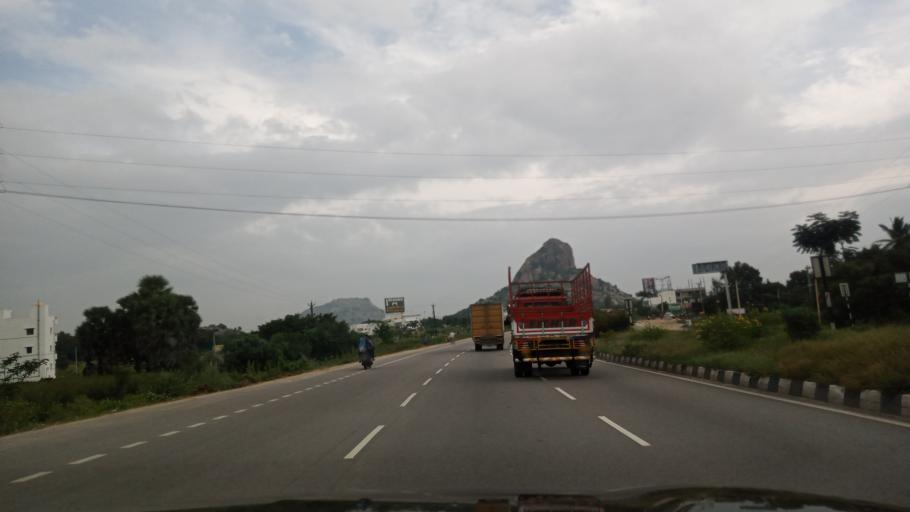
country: IN
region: Tamil Nadu
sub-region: Krishnagiri
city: Krishnagiri
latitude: 12.5578
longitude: 78.1856
